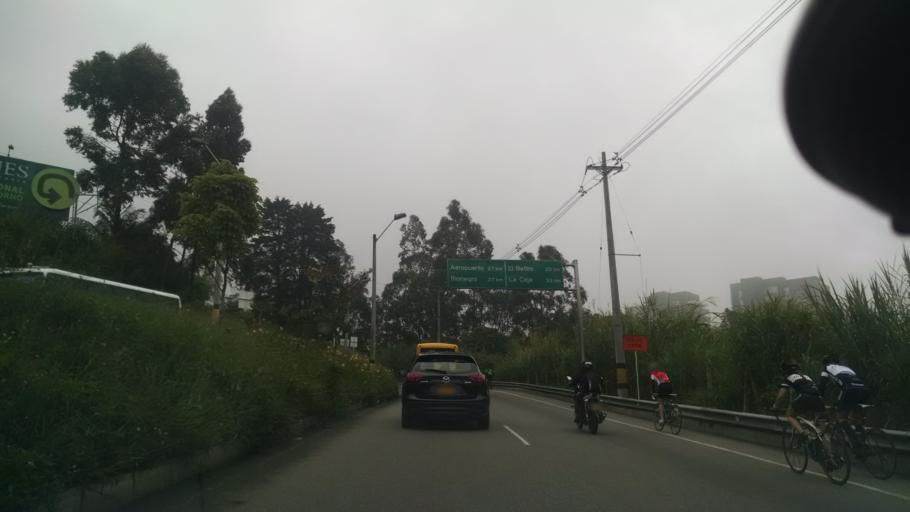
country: CO
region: Antioquia
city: Medellin
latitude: 6.2115
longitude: -75.5468
